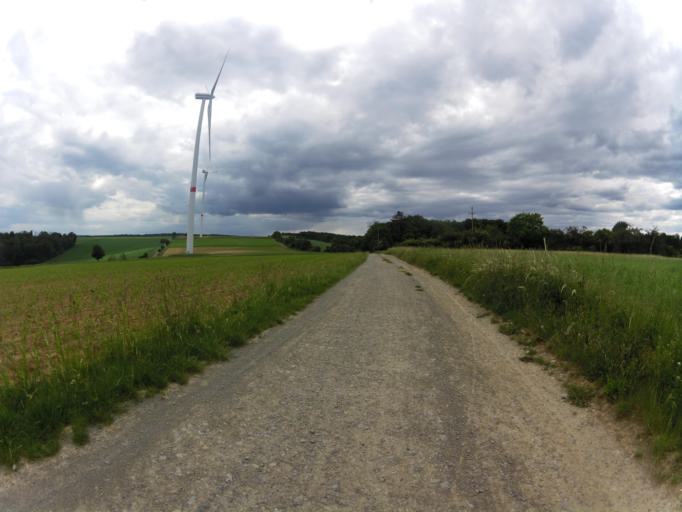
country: DE
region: Bavaria
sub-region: Regierungsbezirk Unterfranken
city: Retzstadt
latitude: 49.8860
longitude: 9.8803
